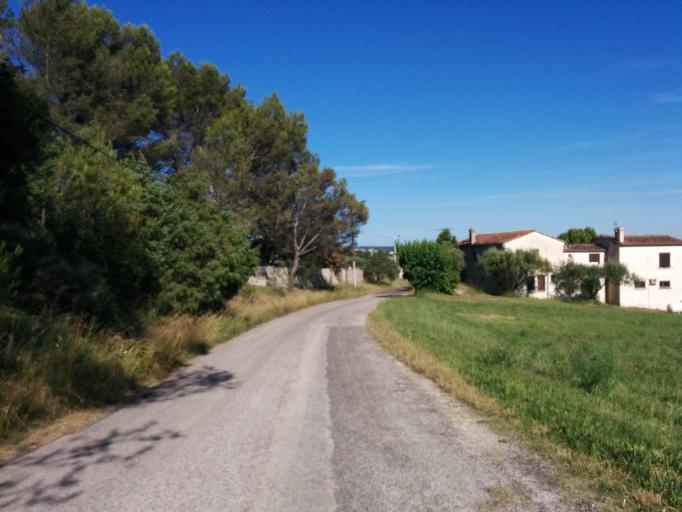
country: FR
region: Languedoc-Roussillon
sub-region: Departement du Gard
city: Saint-Christol-les-Ales
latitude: 44.0922
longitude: 4.0631
